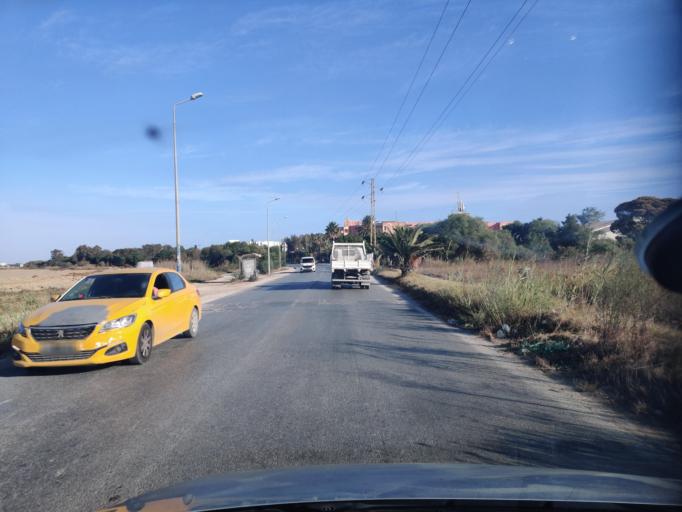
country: TN
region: Tunis
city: Al Marsa
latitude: 36.9373
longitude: 10.2528
